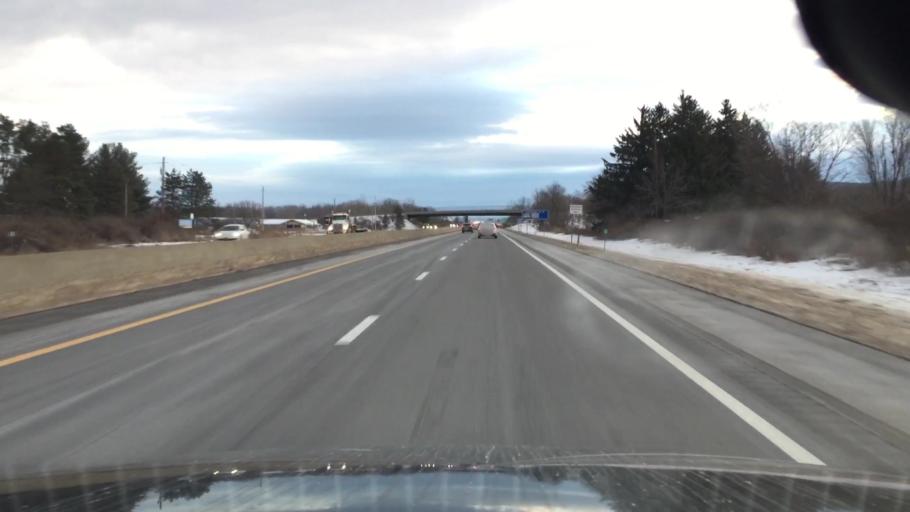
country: US
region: New York
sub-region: Chemung County
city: Big Flats
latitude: 42.1444
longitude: -76.9299
